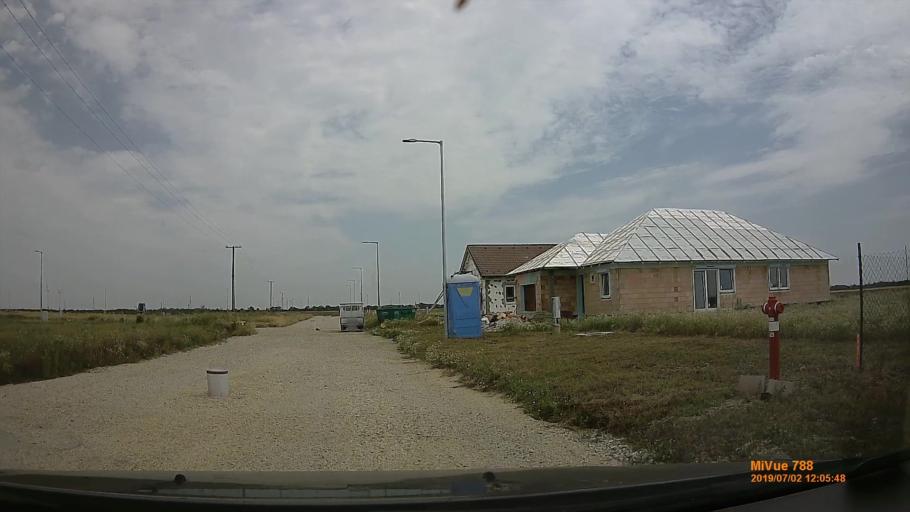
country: HU
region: Gyor-Moson-Sopron
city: Janossomorja
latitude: 47.8520
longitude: 17.1850
